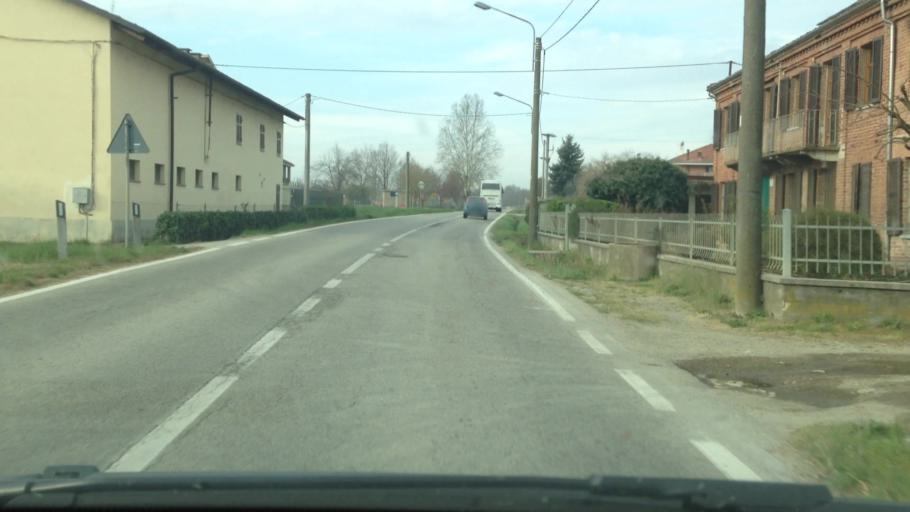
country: IT
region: Piedmont
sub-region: Provincia di Asti
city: Celle Enomondo
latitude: 44.8693
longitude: 8.1114
